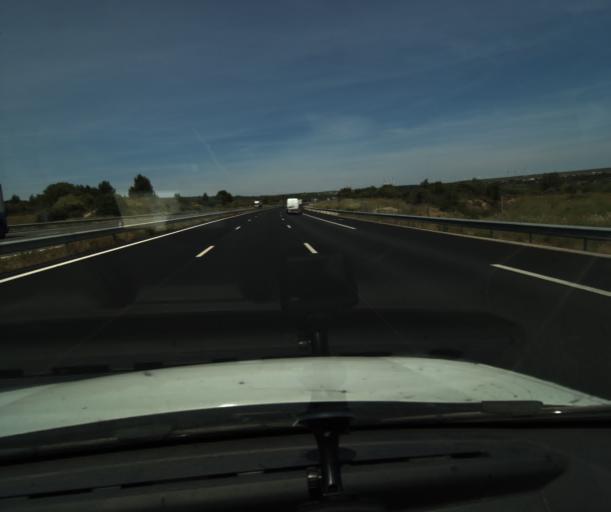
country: FR
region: Languedoc-Roussillon
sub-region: Departement de l'Aude
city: Sigean
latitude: 42.9659
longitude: 2.9688
